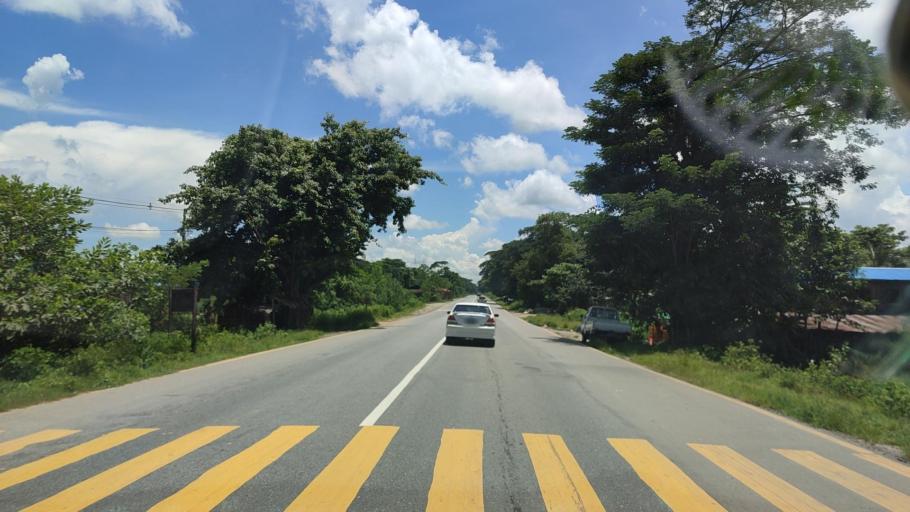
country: MM
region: Bago
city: Pyu
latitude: 18.2152
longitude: 96.5641
